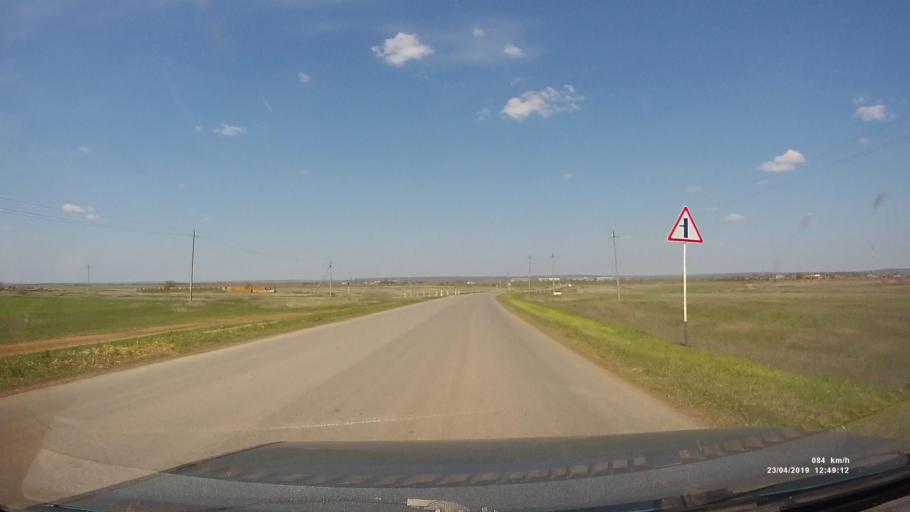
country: RU
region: Kalmykiya
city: Yashalta
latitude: 46.5345
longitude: 42.6388
